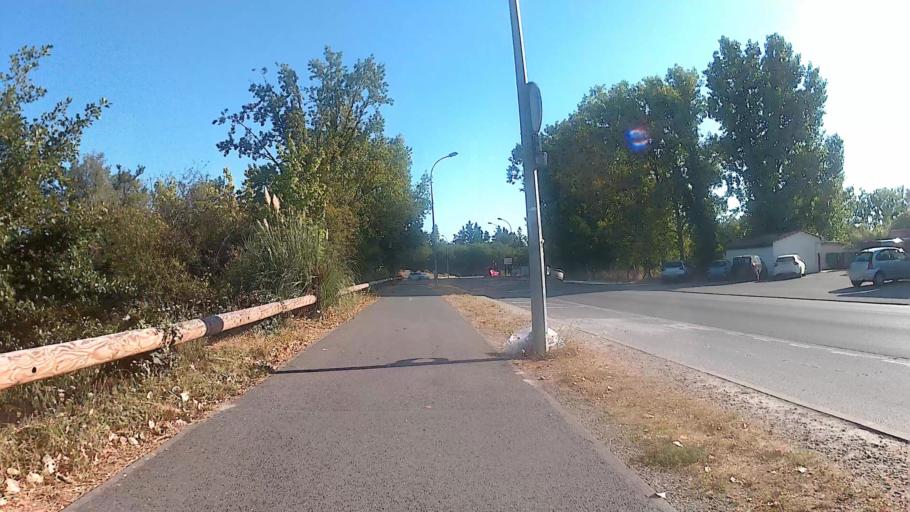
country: FR
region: Aquitaine
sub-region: Departement de la Gironde
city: Villenave-d'Ornon
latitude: 44.7829
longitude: -0.5368
